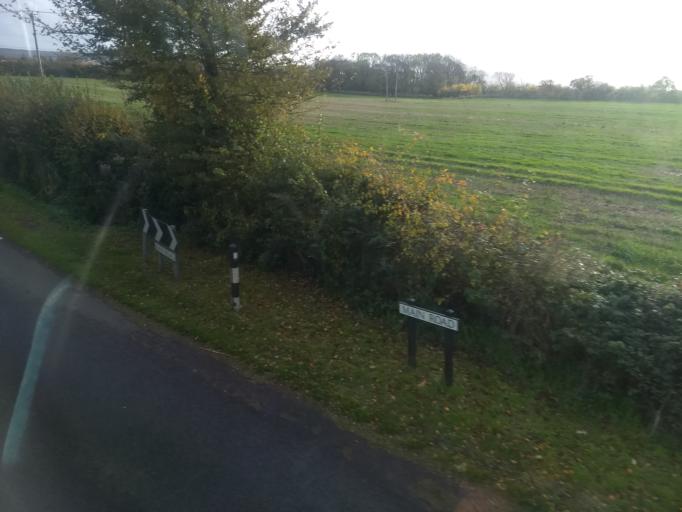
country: GB
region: England
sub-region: Isle of Wight
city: Shalfleet
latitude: 50.6992
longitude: -1.4085
